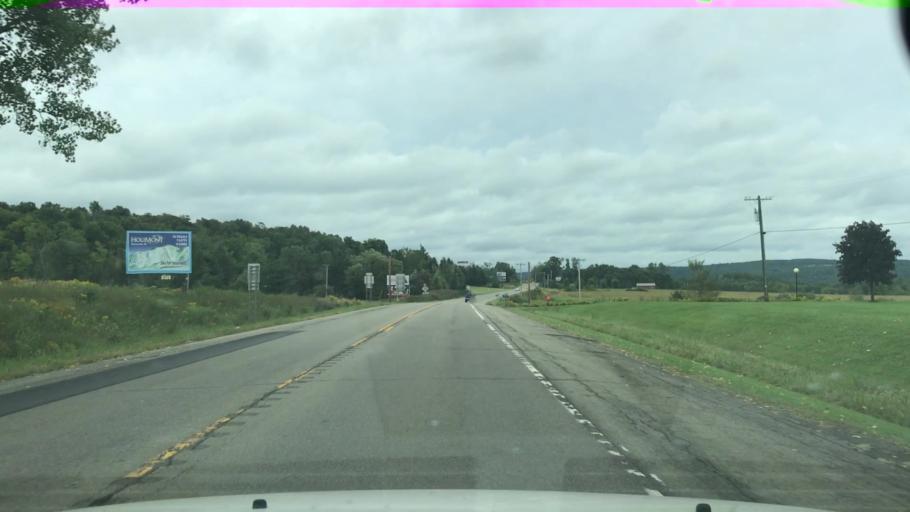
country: US
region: New York
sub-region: Erie County
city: Springville
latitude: 42.4585
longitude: -78.7014
